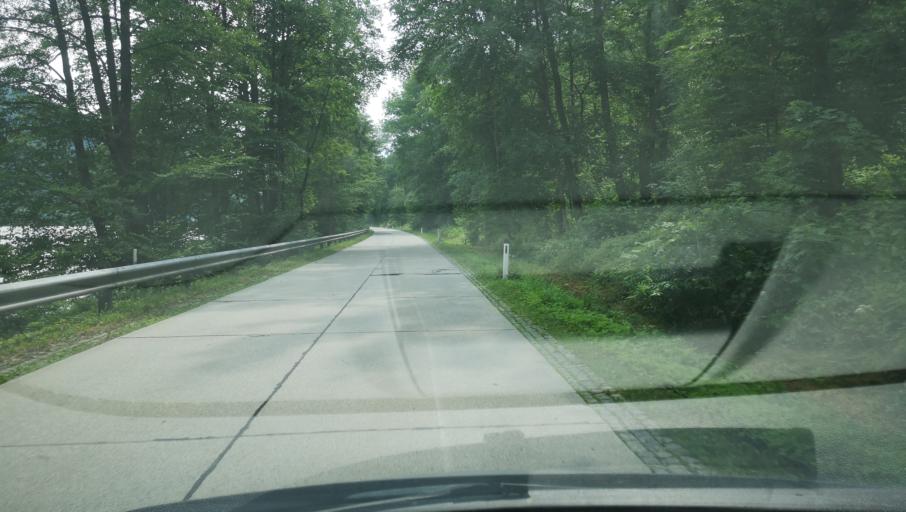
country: AT
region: Lower Austria
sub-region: Politischer Bezirk Melk
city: Nochling
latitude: 48.1940
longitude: 14.9913
